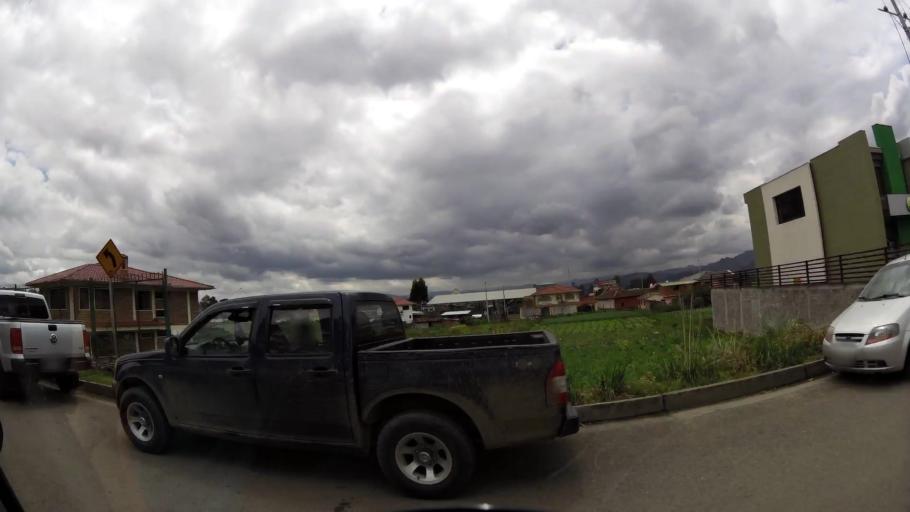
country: EC
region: Azuay
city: Cuenca
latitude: -2.8953
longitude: -79.0548
